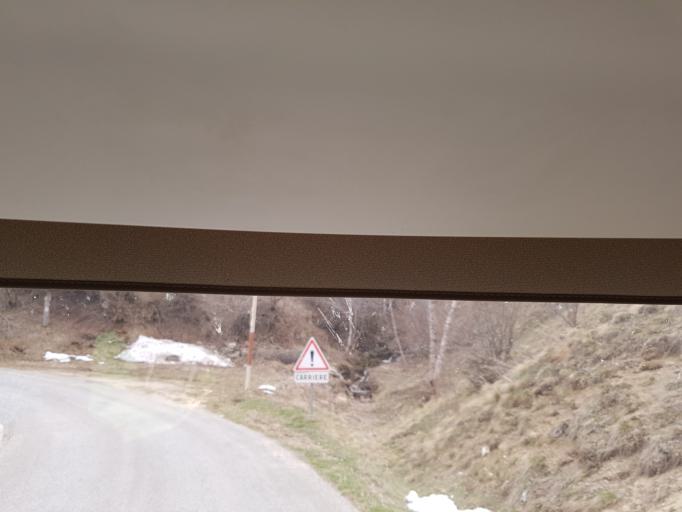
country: FR
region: Languedoc-Roussillon
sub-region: Departement de l'Aude
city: Quillan
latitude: 42.6601
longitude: 2.1239
